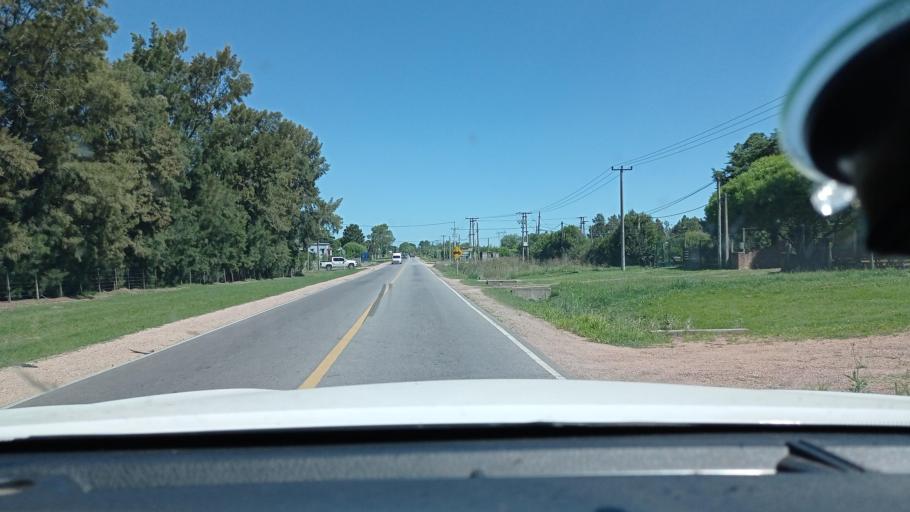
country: UY
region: Canelones
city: La Paz
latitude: -34.7715
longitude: -56.1666
